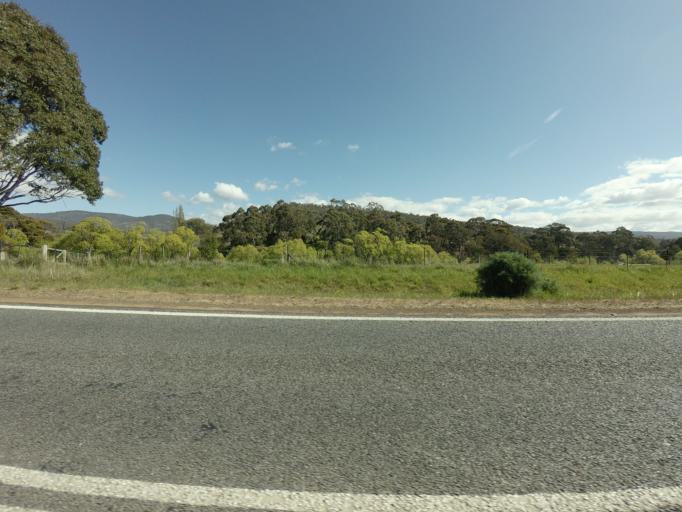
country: AU
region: Tasmania
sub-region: Derwent Valley
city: New Norfolk
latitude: -42.7635
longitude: 147.0155
